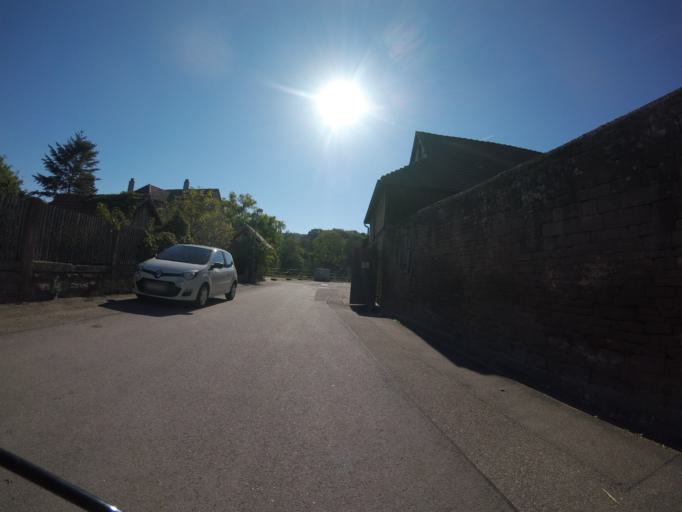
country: DE
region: Baden-Wuerttemberg
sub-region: Karlsruhe Region
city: Illingen
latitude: 48.9914
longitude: 8.9391
